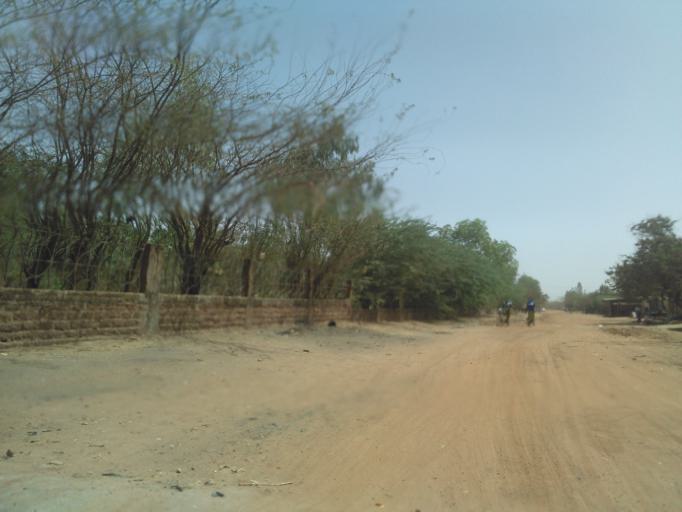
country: BF
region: Centre
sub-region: Kadiogo Province
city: Ouagadougou
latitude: 12.3928
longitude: -1.5716
